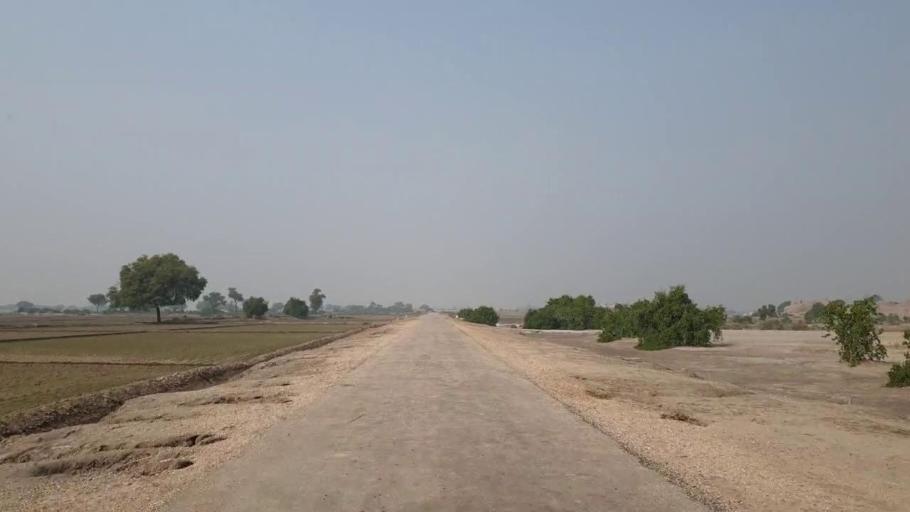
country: PK
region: Sindh
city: Bhan
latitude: 26.5005
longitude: 67.6948
